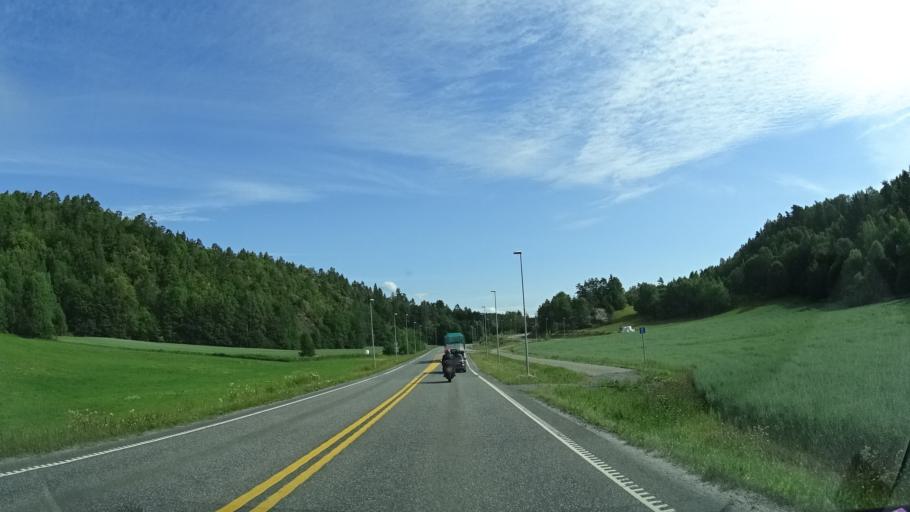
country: NO
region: Telemark
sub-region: Bamble
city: Langesund
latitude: 58.9864
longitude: 9.6255
